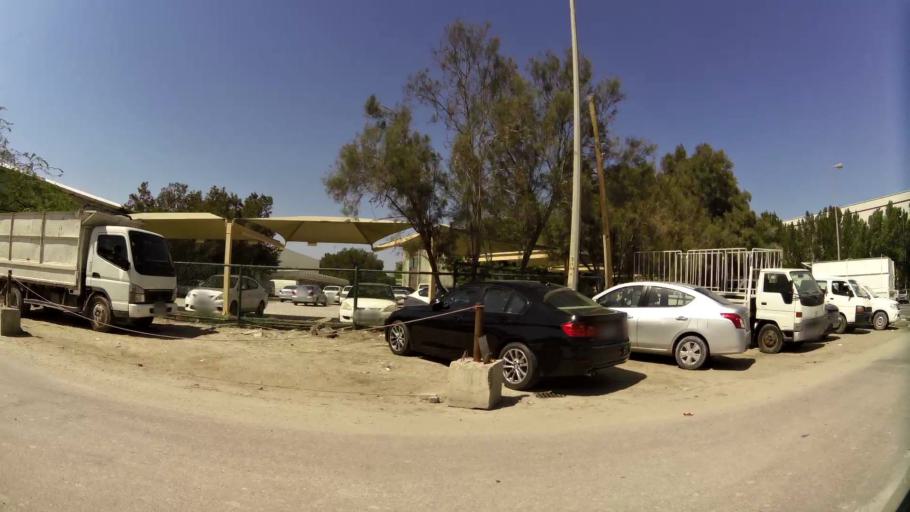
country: BH
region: Manama
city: Manama
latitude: 26.1973
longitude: 50.5982
